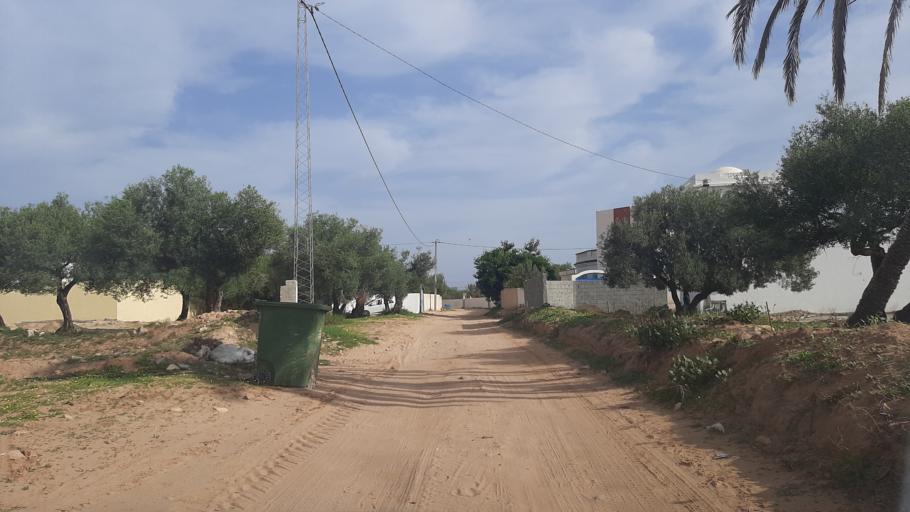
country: TN
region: Madanin
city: Midoun
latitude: 33.8101
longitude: 11.0249
